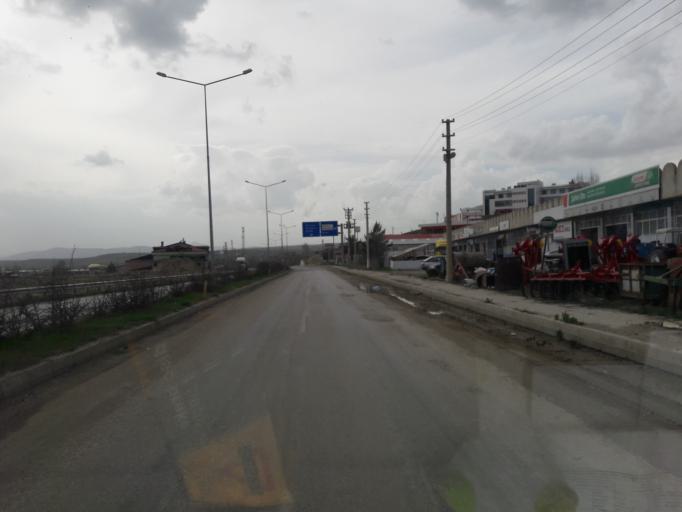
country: TR
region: Gumushane
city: Siran
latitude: 40.1780
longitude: 39.1265
